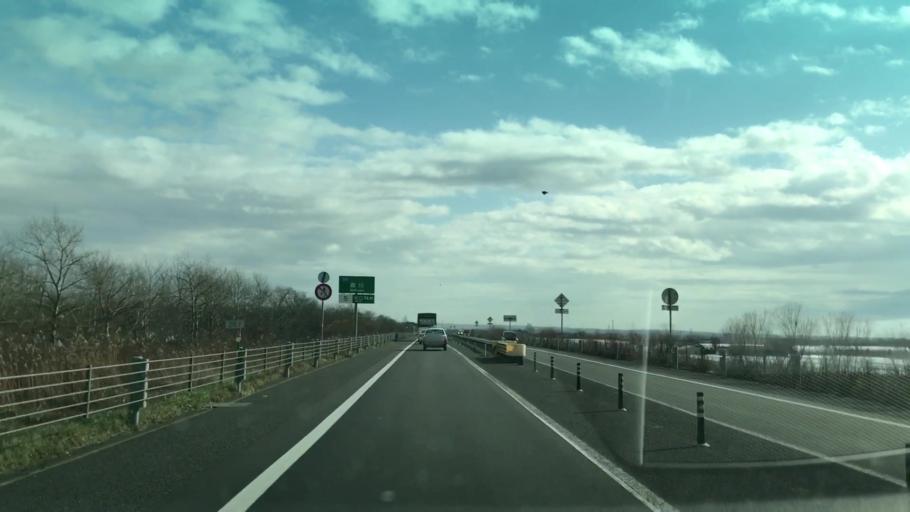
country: JP
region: Hokkaido
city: Tomakomai
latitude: 42.5937
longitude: 141.9112
